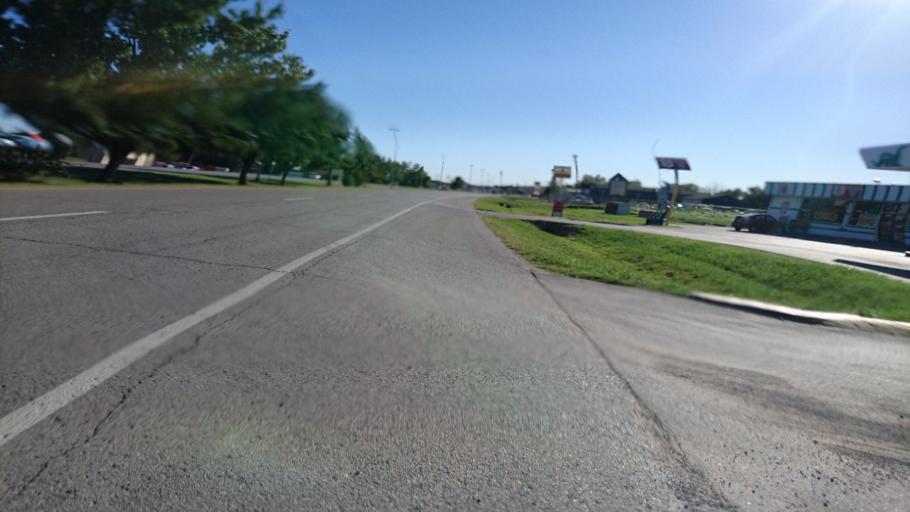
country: US
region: Oklahoma
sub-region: Rogers County
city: Claremore
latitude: 36.3260
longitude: -95.6073
